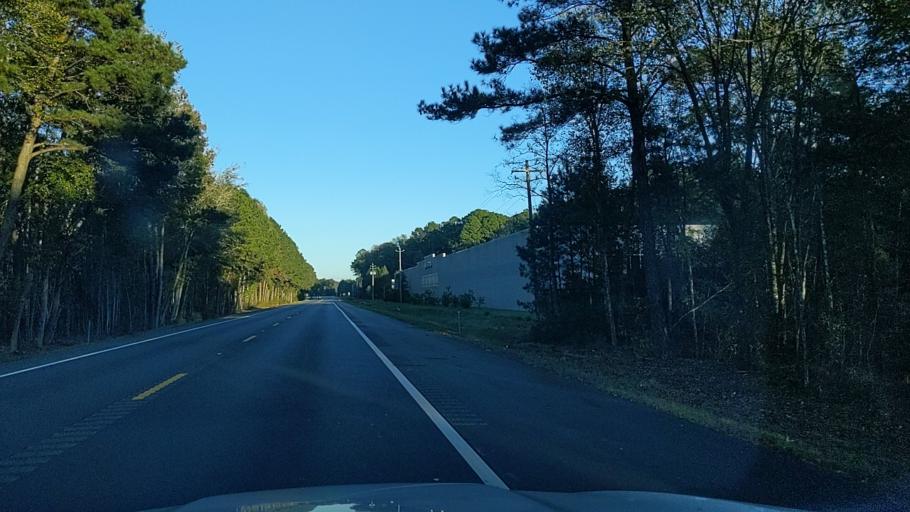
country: US
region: Georgia
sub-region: Chatham County
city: Port Wentworth
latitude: 32.1962
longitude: -81.2093
